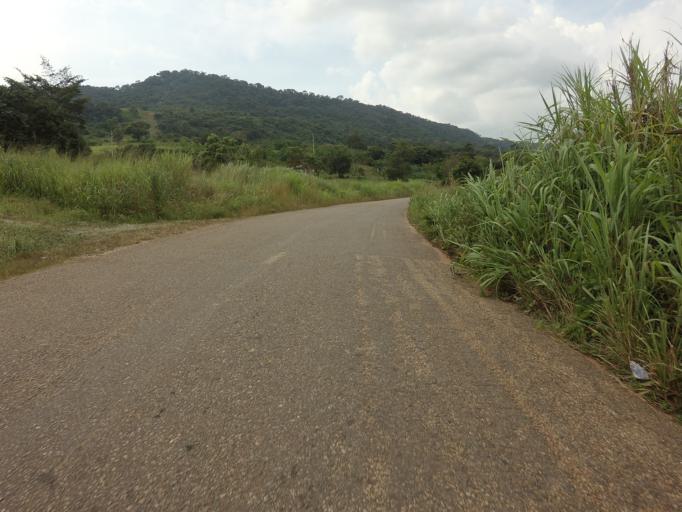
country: GH
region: Volta
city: Ho
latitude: 6.6440
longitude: 0.3374
